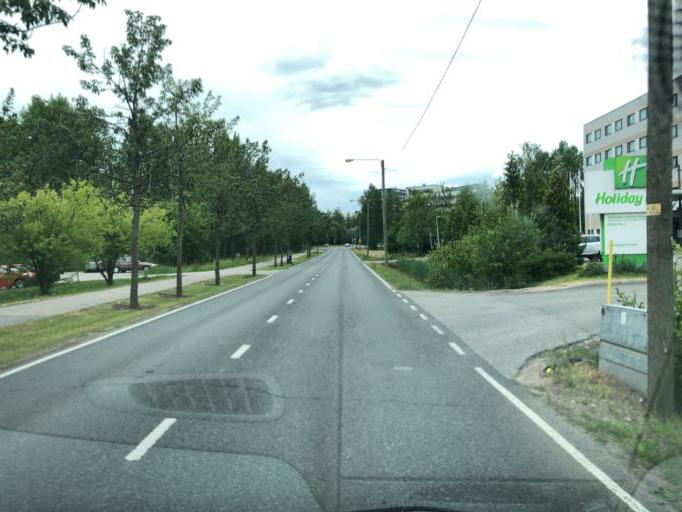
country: FI
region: Uusimaa
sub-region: Helsinki
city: Vantaa
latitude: 60.2958
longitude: 24.9724
